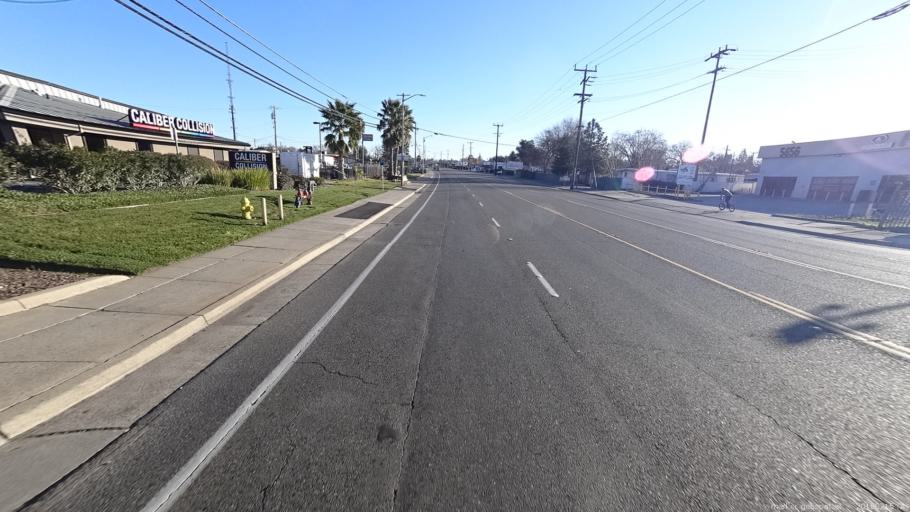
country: US
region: California
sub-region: Sacramento County
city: Foothill Farms
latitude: 38.6694
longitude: -121.3340
